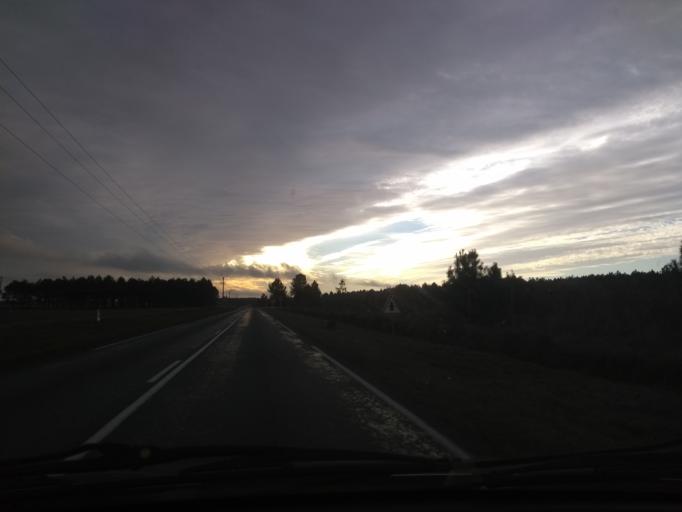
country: FR
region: Aquitaine
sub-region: Departement de la Gironde
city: Saucats
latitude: 44.6214
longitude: -0.6705
